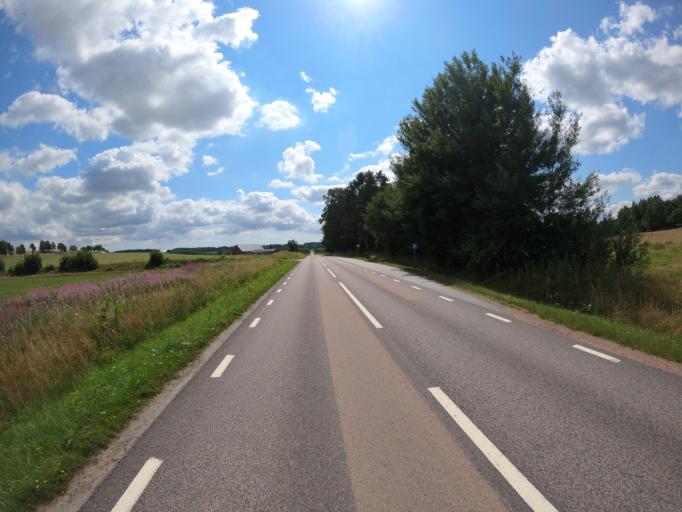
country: SE
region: Skane
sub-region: Lunds Kommun
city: Veberod
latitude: 55.6034
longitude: 13.4890
